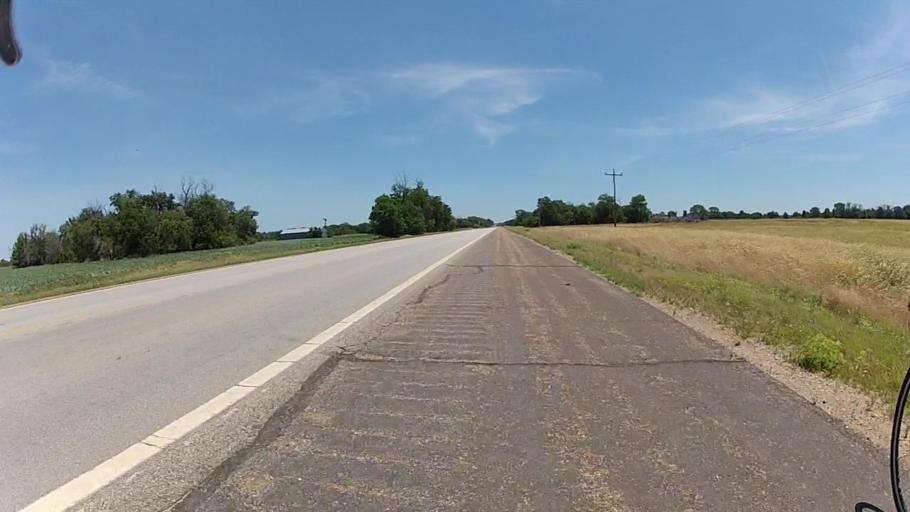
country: US
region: Kansas
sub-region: Barber County
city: Medicine Lodge
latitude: 37.2534
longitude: -98.3373
